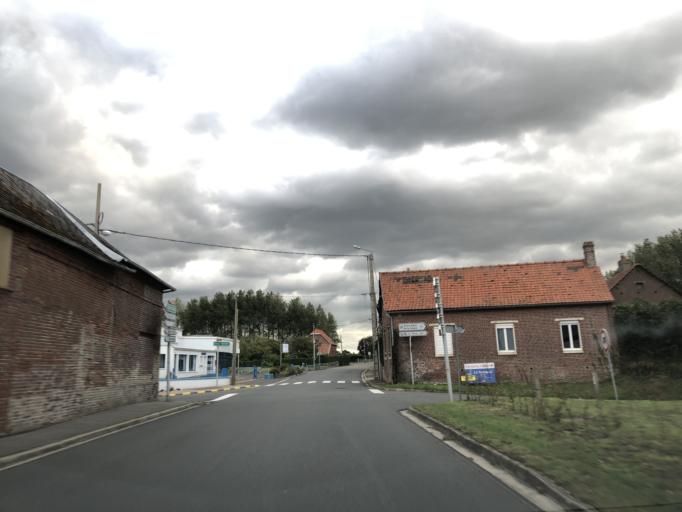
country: FR
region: Picardie
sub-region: Departement de la Somme
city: Ault
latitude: 50.0763
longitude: 1.4354
